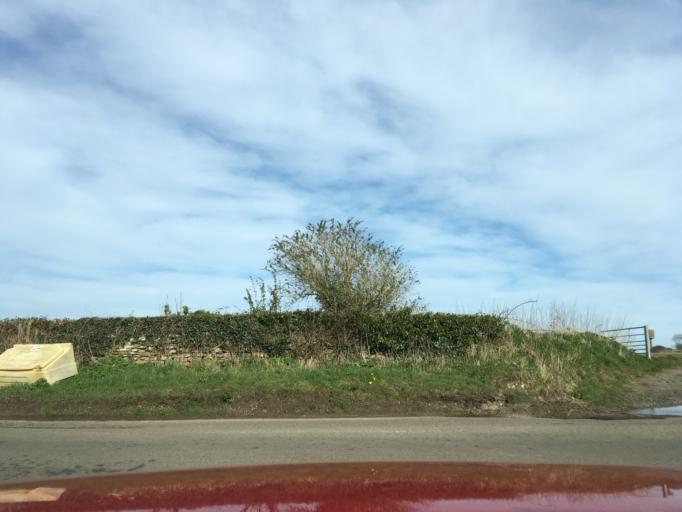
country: GB
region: England
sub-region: Wiltshire
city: Luckington
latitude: 51.5463
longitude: -2.2272
